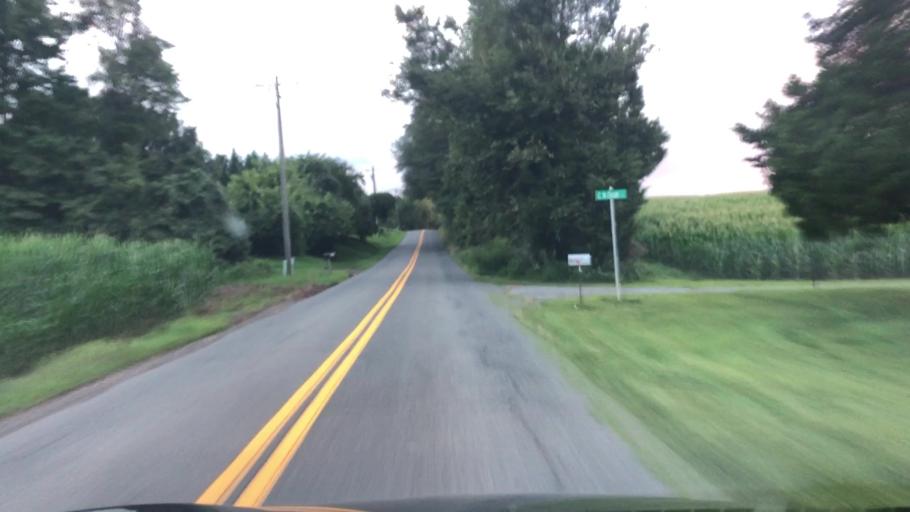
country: US
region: Virginia
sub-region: Stafford County
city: Falmouth
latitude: 38.4496
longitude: -77.5880
